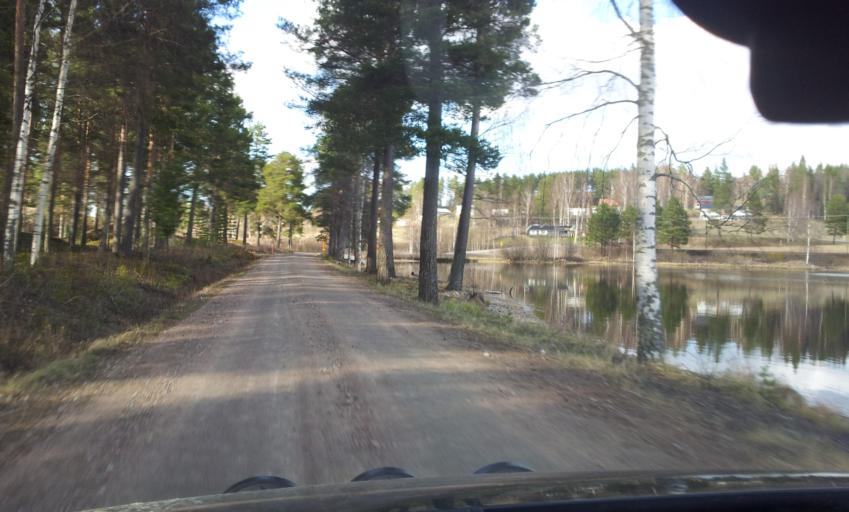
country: SE
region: Vaesternorrland
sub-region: Ange Kommun
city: Ange
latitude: 62.1519
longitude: 15.6733
